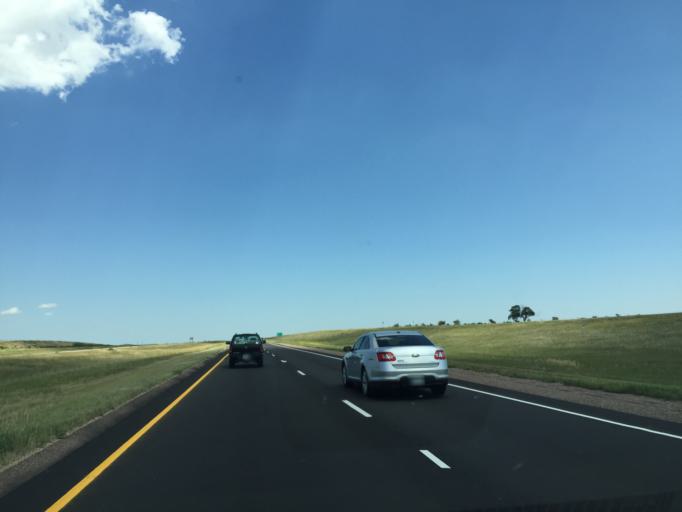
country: US
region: Colorado
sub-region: Lincoln County
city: Hugo
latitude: 39.2796
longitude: -103.3825
